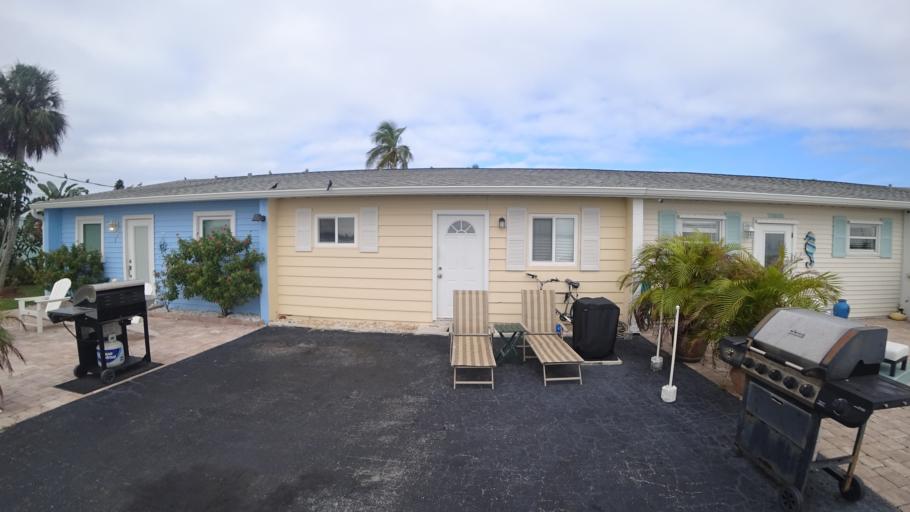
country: US
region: Florida
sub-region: Manatee County
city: Longboat Key
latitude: 27.4176
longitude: -82.6550
